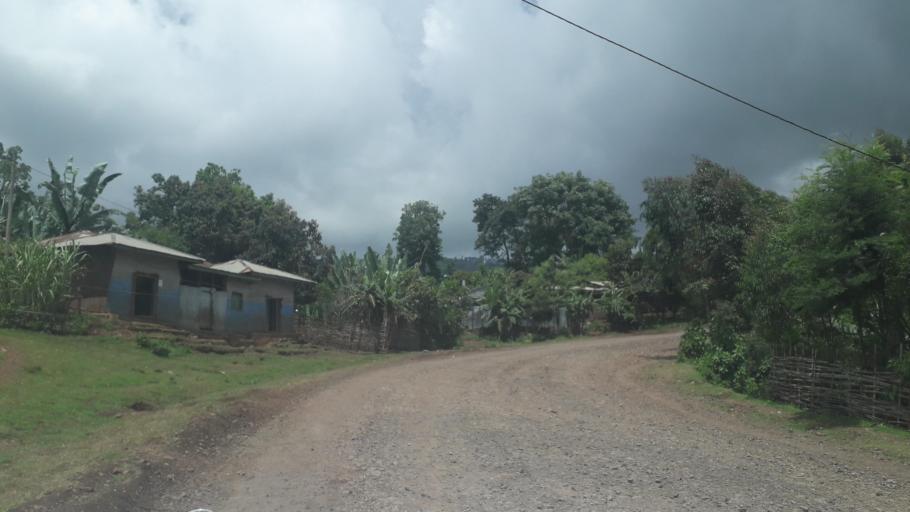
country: ET
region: Oromiya
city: Jima
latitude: 7.4251
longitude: 36.8719
